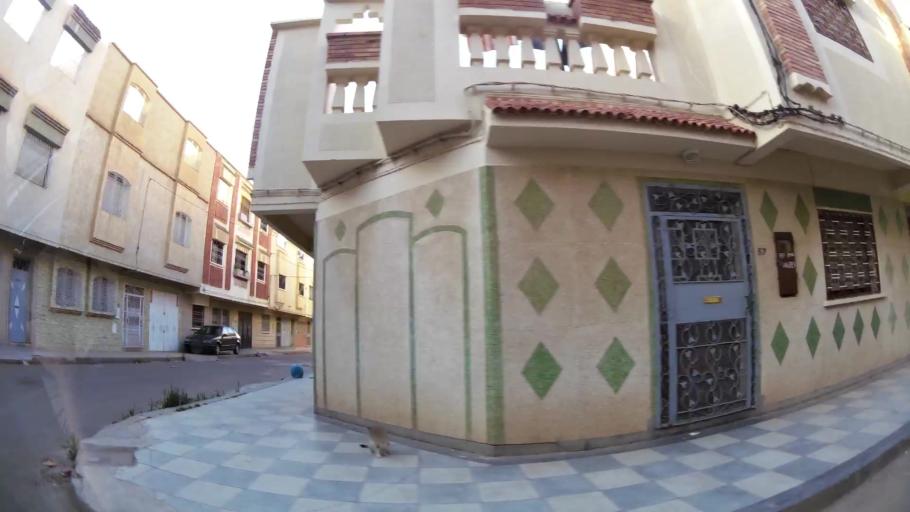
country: MA
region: Oriental
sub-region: Oujda-Angad
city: Oujda
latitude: 34.6744
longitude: -1.8929
